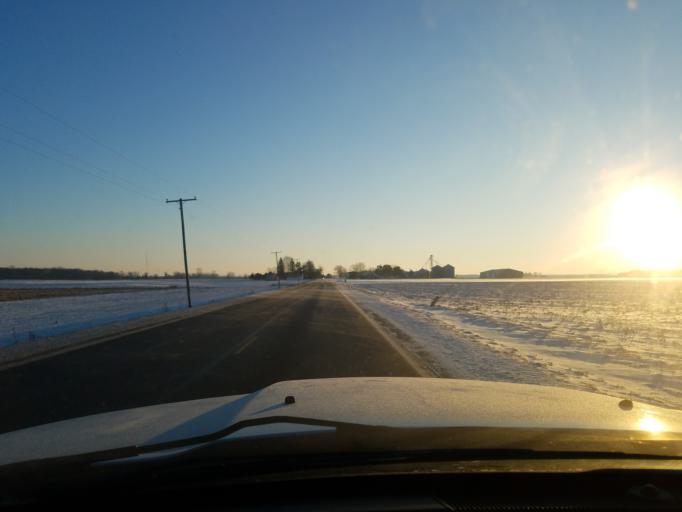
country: US
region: Indiana
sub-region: Marshall County
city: Bremen
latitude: 41.4499
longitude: -86.2262
